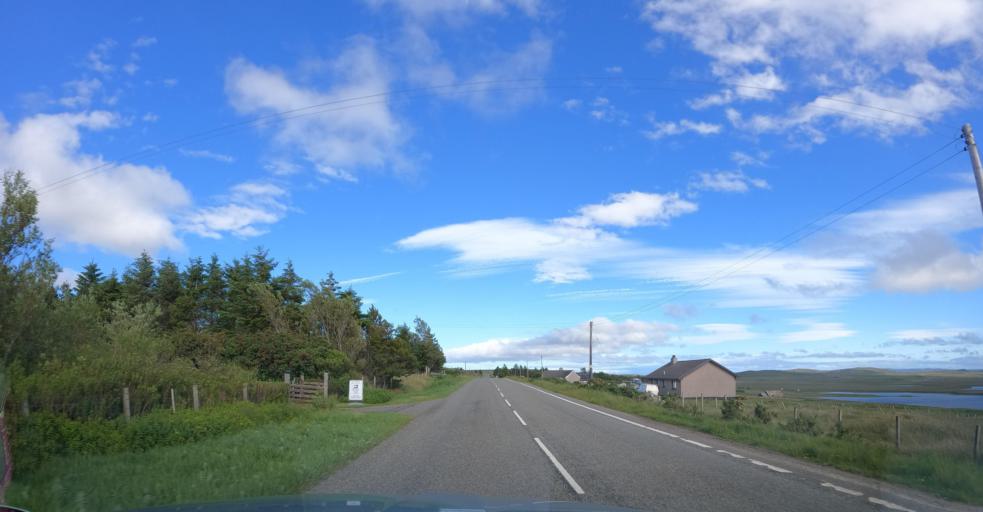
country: GB
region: Scotland
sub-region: Eilean Siar
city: Stornoway
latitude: 58.1720
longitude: -6.5822
